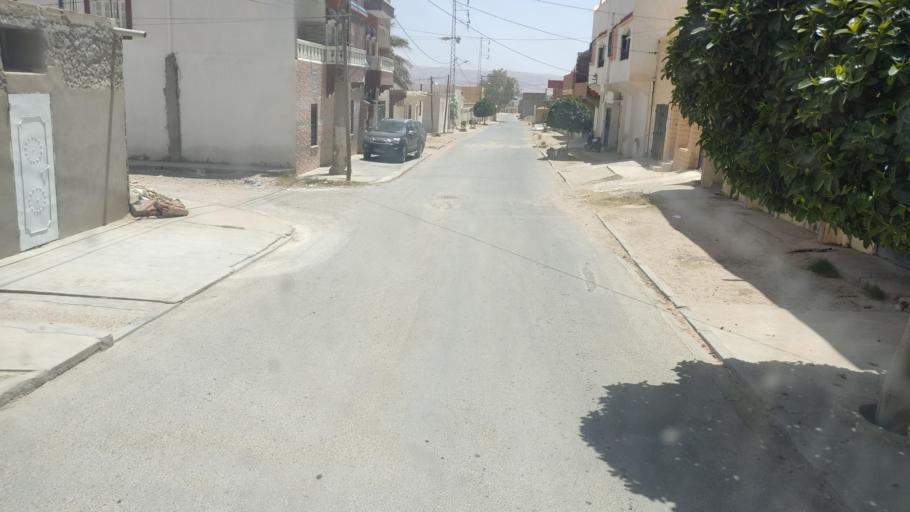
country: TN
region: Gafsa
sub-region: Gafsa Municipality
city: Gafsa
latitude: 34.3390
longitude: 8.9422
